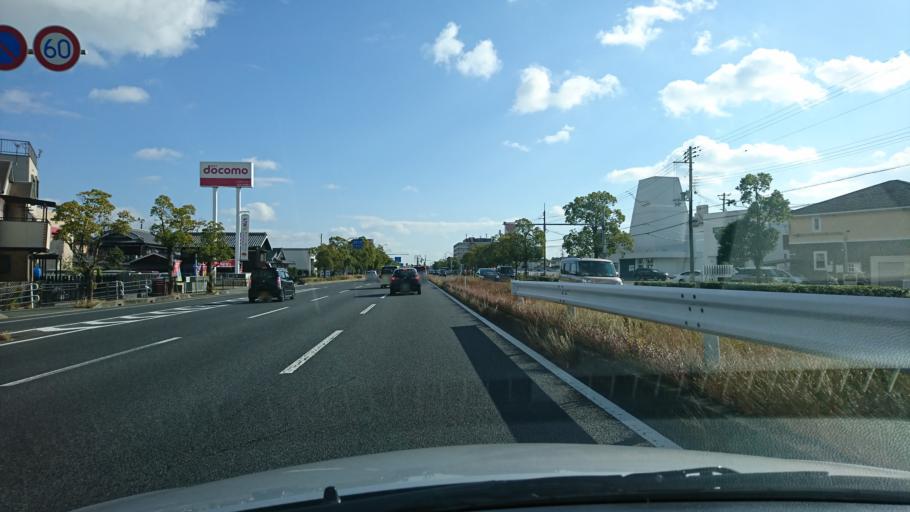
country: JP
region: Hyogo
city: Kakogawacho-honmachi
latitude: 34.7383
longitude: 134.8483
